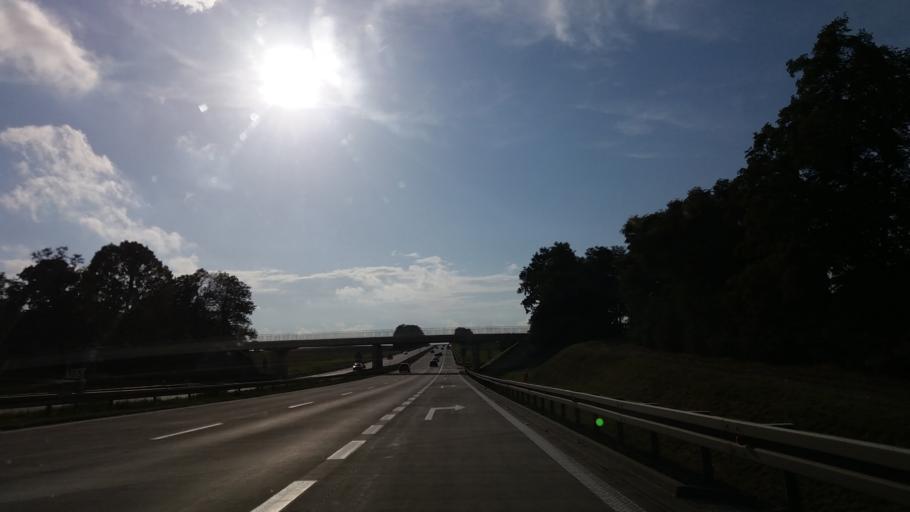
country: PL
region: Lower Silesian Voivodeship
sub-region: Powiat legnicki
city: Legnickie Pole
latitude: 51.1282
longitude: 16.3432
